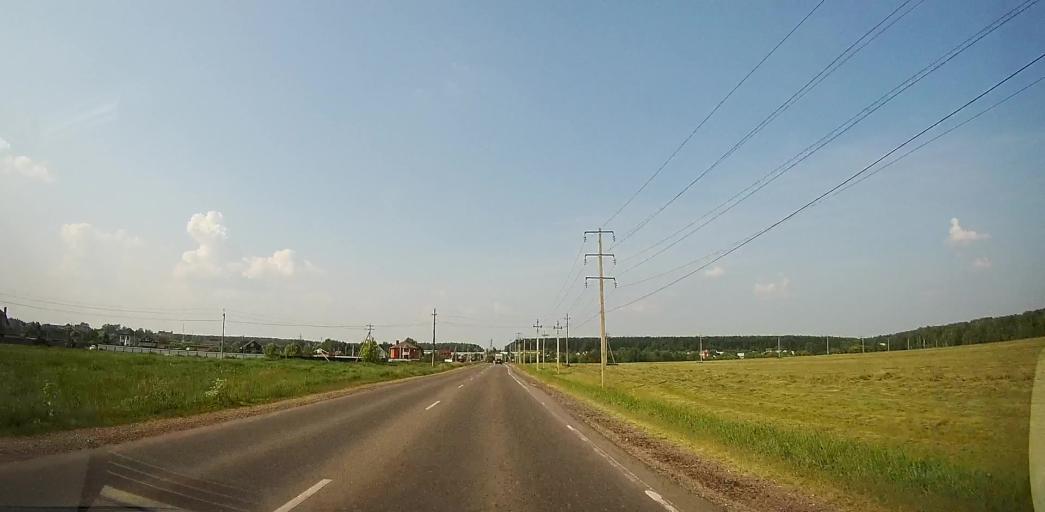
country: RU
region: Moskovskaya
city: Barybino
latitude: 55.2702
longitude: 37.9156
